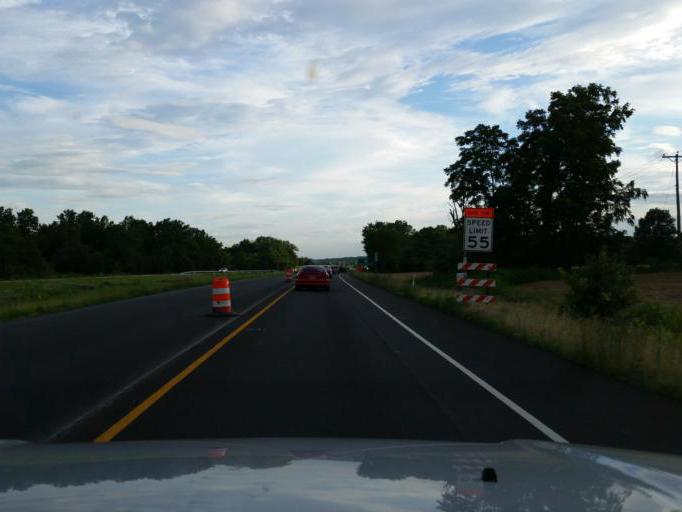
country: US
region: Pennsylvania
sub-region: Adams County
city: Lake Heritage
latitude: 39.7819
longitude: -77.2227
